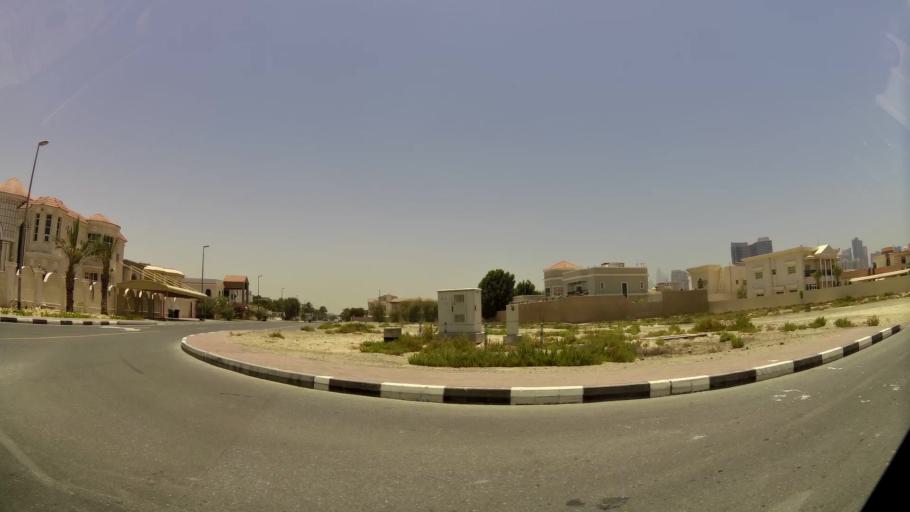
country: AE
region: Dubai
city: Dubai
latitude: 25.0967
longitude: 55.1917
